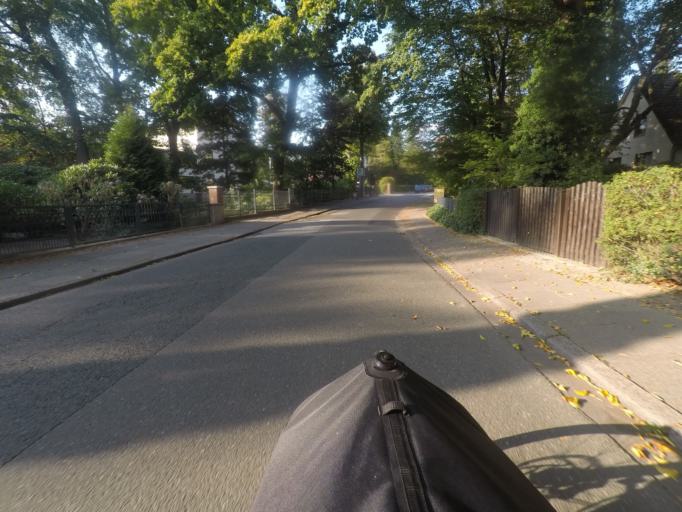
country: DE
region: Schleswig-Holstein
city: Barsbuettel
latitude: 53.6102
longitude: 10.1638
